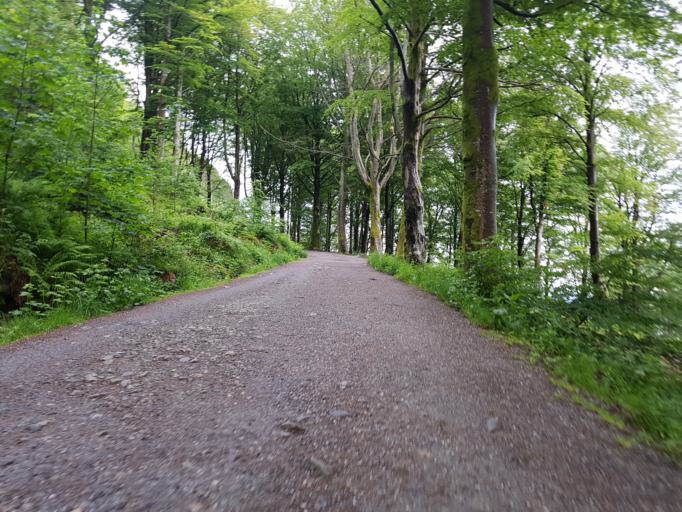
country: NO
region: Hordaland
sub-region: Bergen
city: Bergen
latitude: 60.3964
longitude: 5.3369
